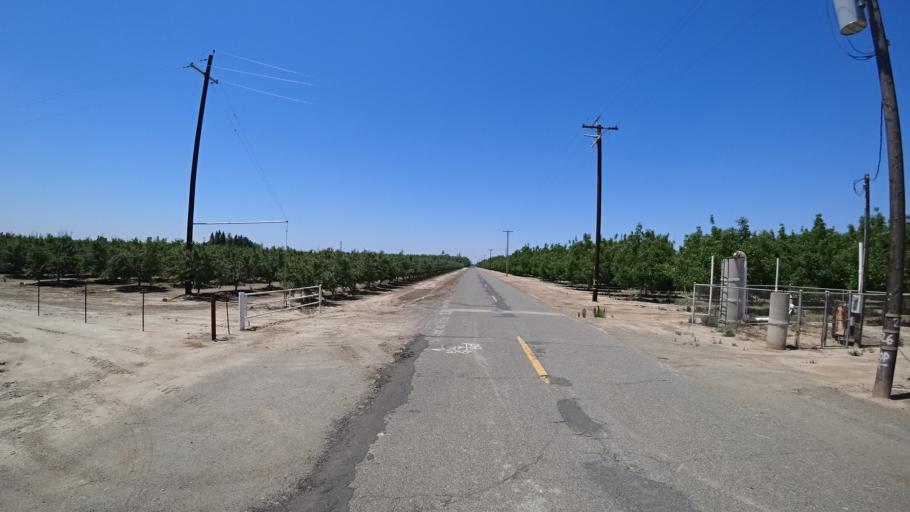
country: US
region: California
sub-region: Fresno County
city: Kingsburg
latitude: 36.4452
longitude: -119.5870
